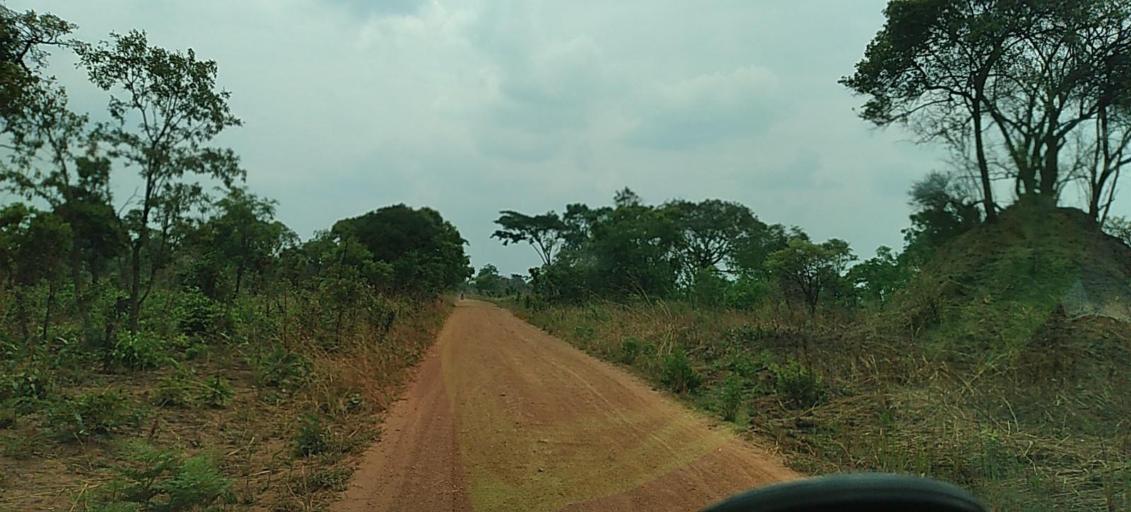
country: ZM
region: North-Western
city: Kansanshi
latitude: -12.0799
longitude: 26.3591
